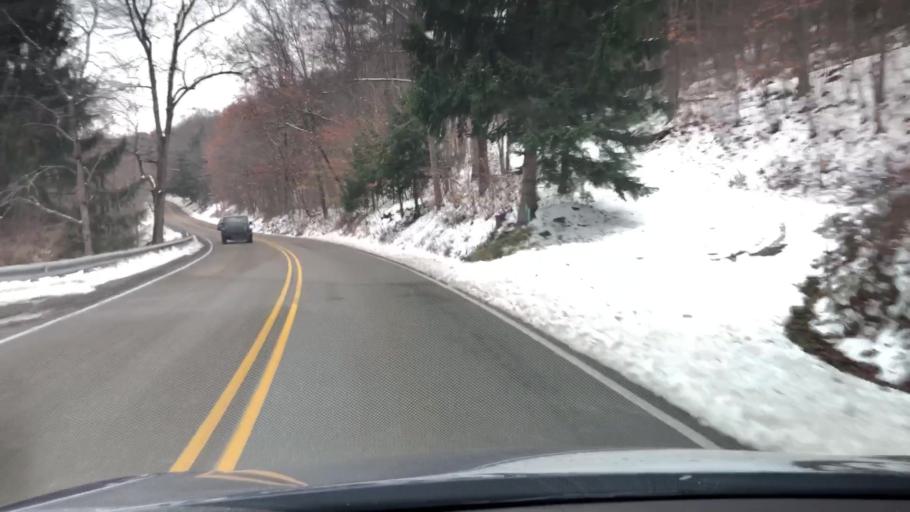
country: US
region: Pennsylvania
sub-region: Elk County
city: Saint Marys
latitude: 41.2842
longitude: -78.4633
